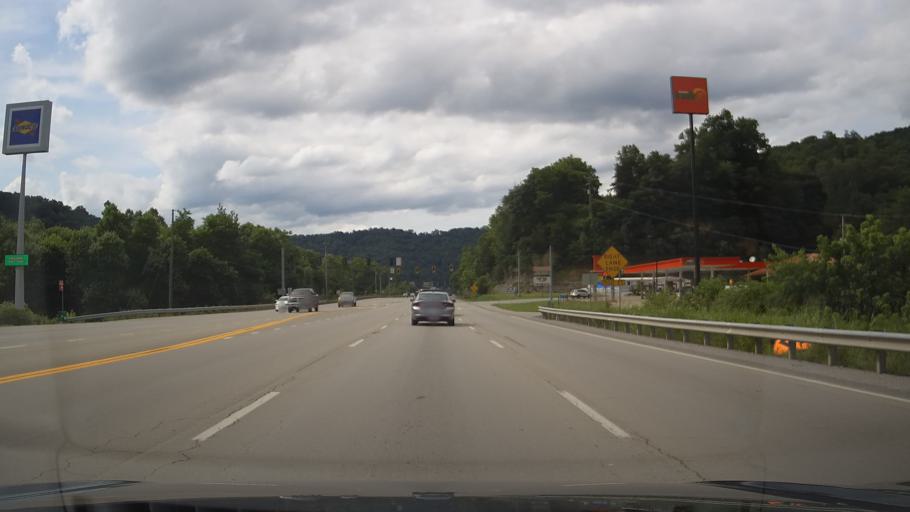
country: US
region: Kentucky
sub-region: Pike County
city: Coal Run Village
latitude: 37.5286
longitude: -82.5751
